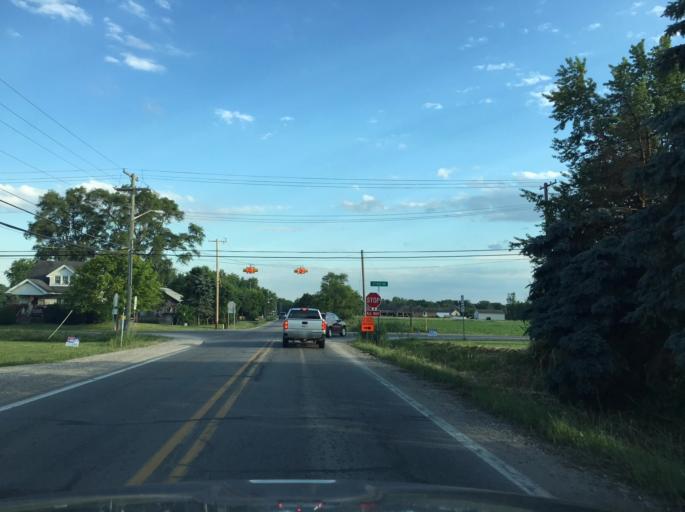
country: US
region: Michigan
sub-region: Macomb County
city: Romeo
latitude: 42.7607
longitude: -82.9611
